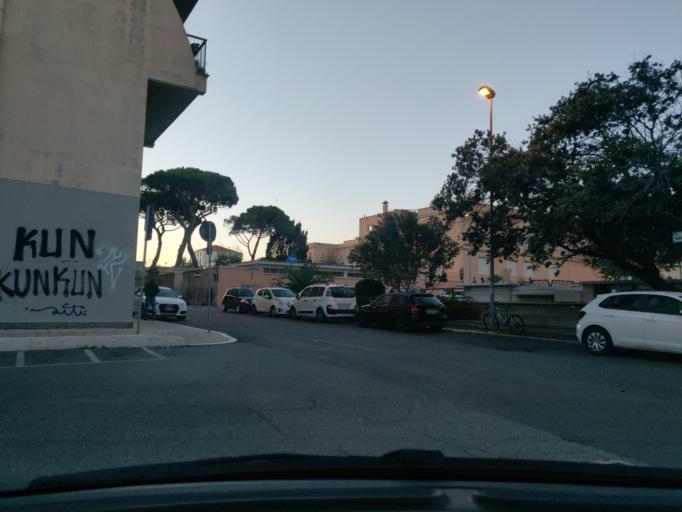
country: IT
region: Latium
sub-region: Citta metropolitana di Roma Capitale
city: Civitavecchia
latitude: 42.0895
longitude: 11.7981
